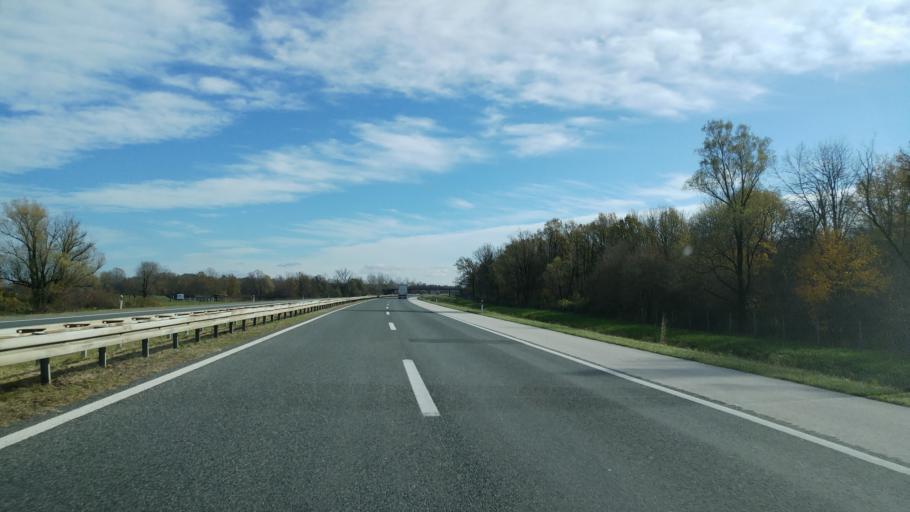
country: HR
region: Sisacko-Moslavacka
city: Husain
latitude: 45.4461
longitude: 16.8119
